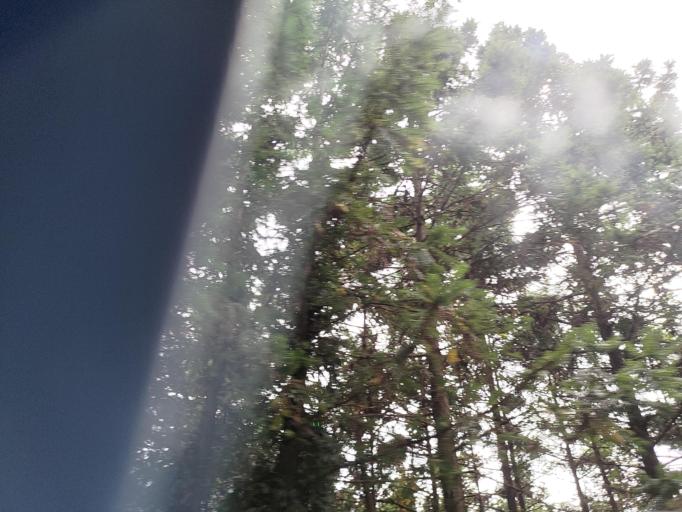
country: TW
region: Taiwan
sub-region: Hsinchu
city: Hsinchu
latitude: 24.6290
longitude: 121.0647
